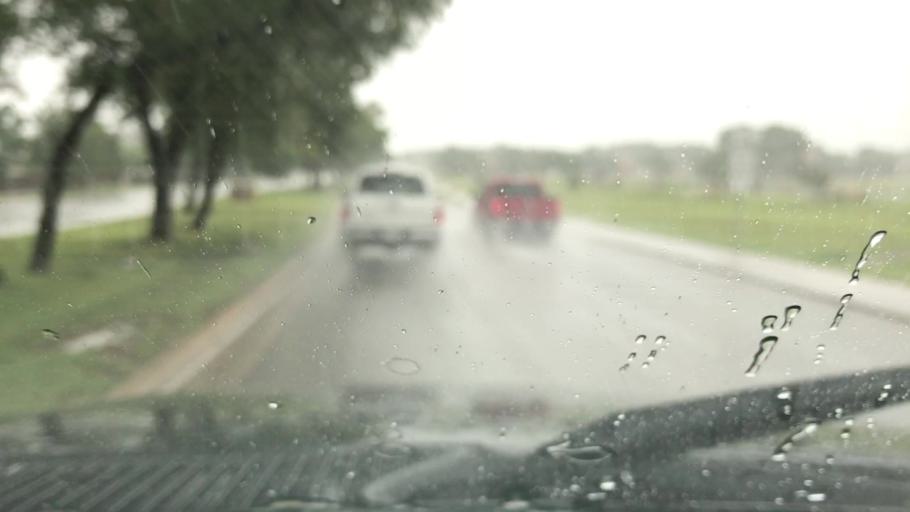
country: US
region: Texas
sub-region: Williamson County
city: Leander
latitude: 30.5376
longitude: -97.8615
